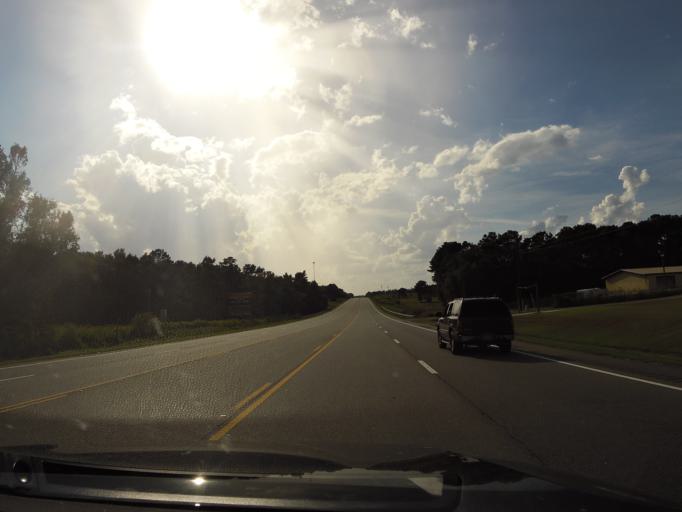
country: US
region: Georgia
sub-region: Brooks County
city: Quitman
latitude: 30.7858
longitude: -83.5968
